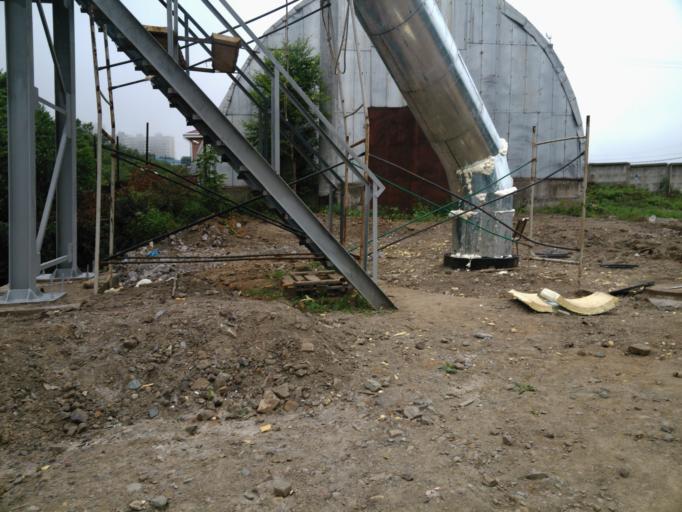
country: RU
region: Primorskiy
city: Vladivostok
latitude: 43.1003
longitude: 131.9839
